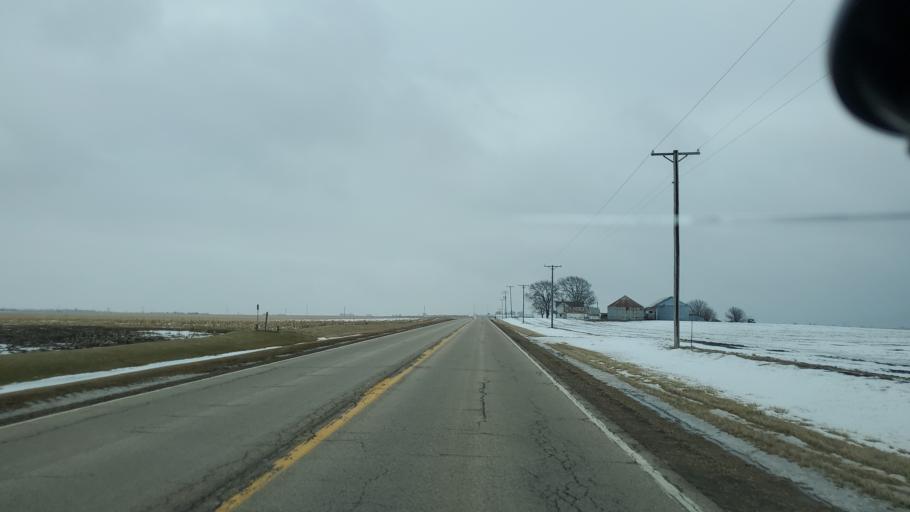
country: US
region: Illinois
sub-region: Marshall County
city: Wenona
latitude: 41.1189
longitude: -89.0957
